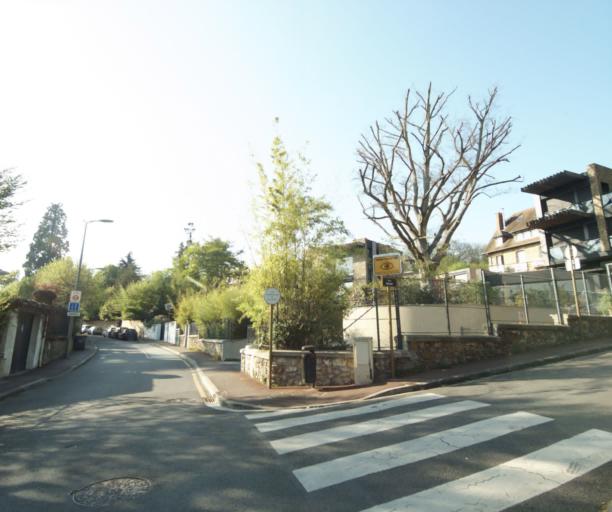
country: FR
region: Ile-de-France
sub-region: Departement des Hauts-de-Seine
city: Sevres
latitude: 48.8276
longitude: 2.2067
